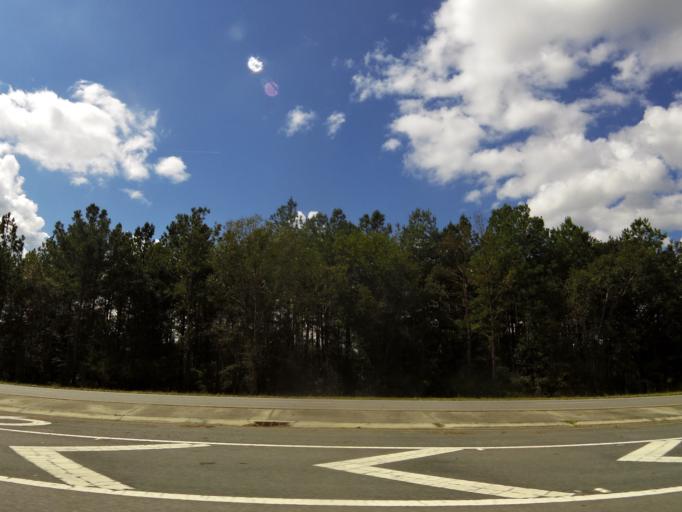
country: US
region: Georgia
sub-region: Charlton County
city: Folkston
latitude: 30.7910
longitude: -81.9830
